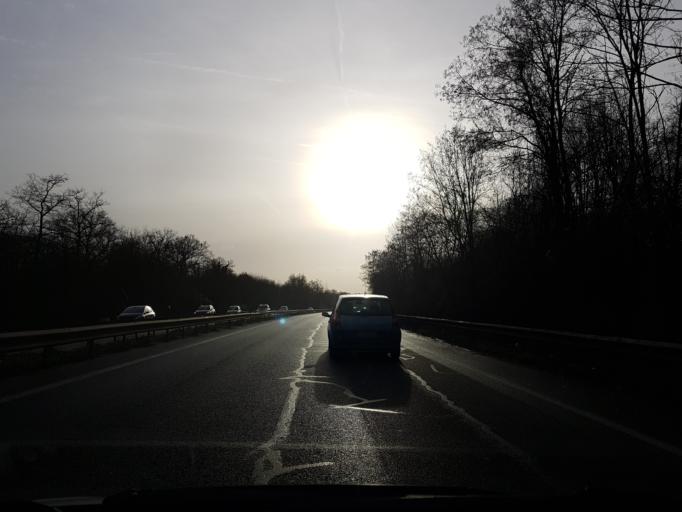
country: FR
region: Ile-de-France
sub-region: Departement de Seine-et-Marne
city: Lieusaint
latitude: 48.6490
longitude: 2.5314
